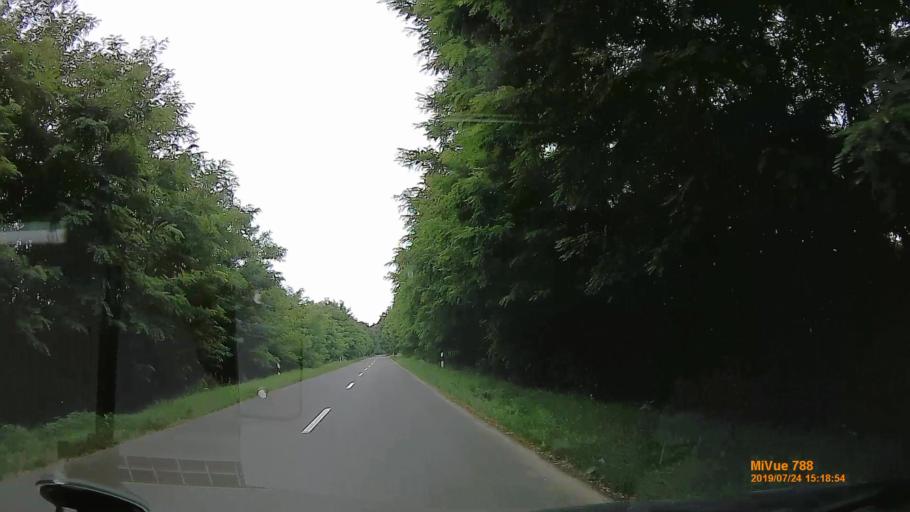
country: HU
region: Szabolcs-Szatmar-Bereg
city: Tarpa
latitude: 48.1759
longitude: 22.5457
